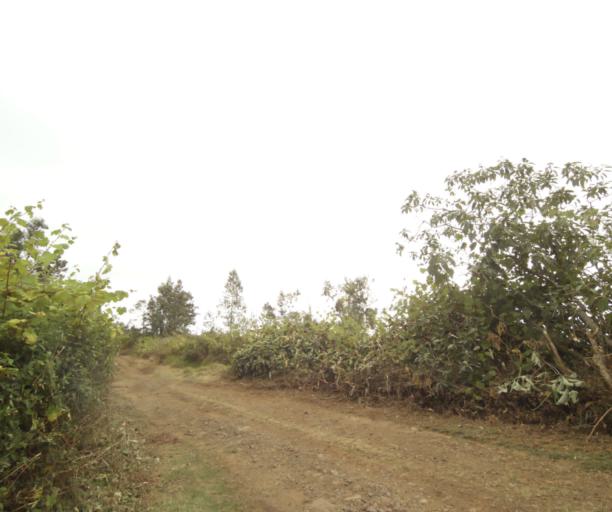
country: RE
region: Reunion
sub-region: Reunion
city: La Possession
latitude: -21.0118
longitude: 55.3607
